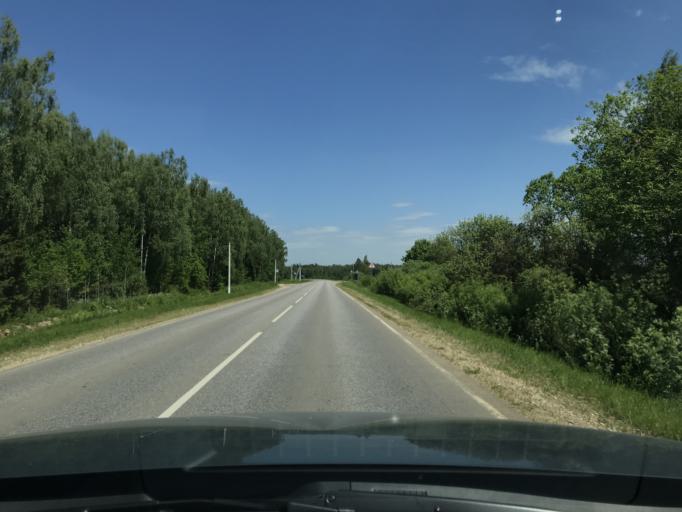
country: RU
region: Moskovskaya
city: Vereya
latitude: 55.3227
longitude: 36.3175
